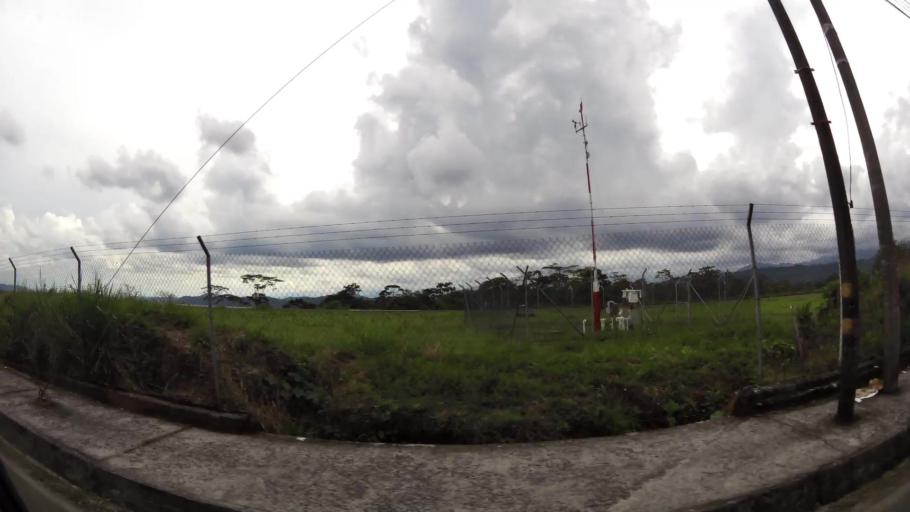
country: EC
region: Pastaza
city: Puyo
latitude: -1.5080
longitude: -78.0568
